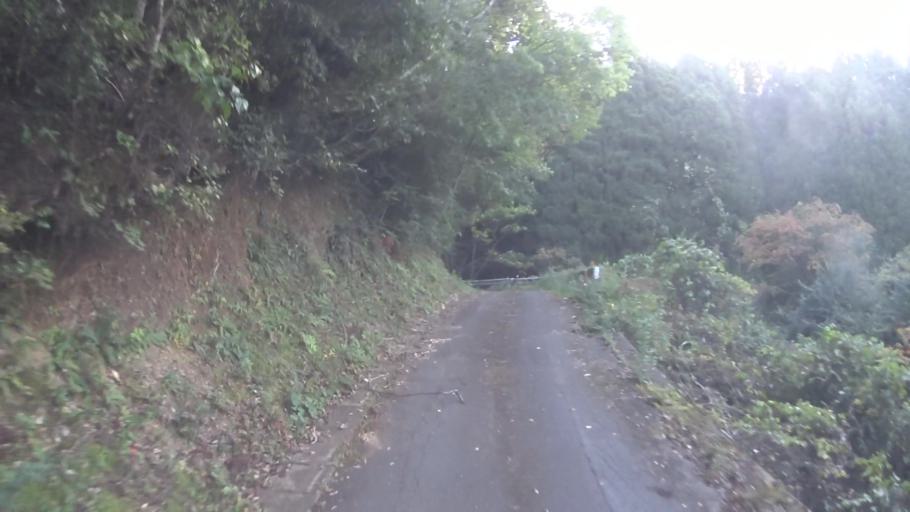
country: JP
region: Kyoto
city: Ayabe
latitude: 35.2719
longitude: 135.2491
